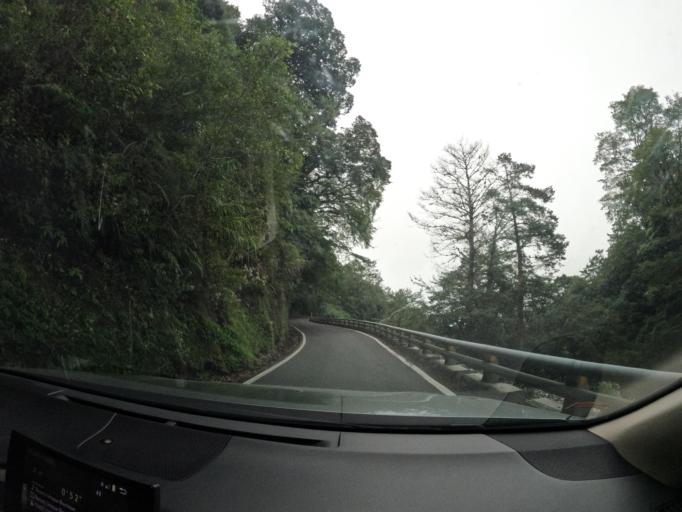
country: TW
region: Taiwan
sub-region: Taitung
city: Taitung
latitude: 23.2410
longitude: 120.9853
